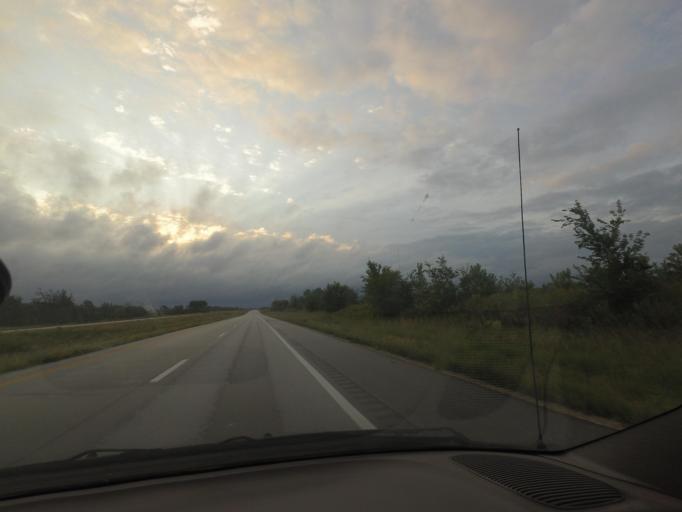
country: US
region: Missouri
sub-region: Shelby County
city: Shelbina
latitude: 39.6817
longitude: -91.9888
